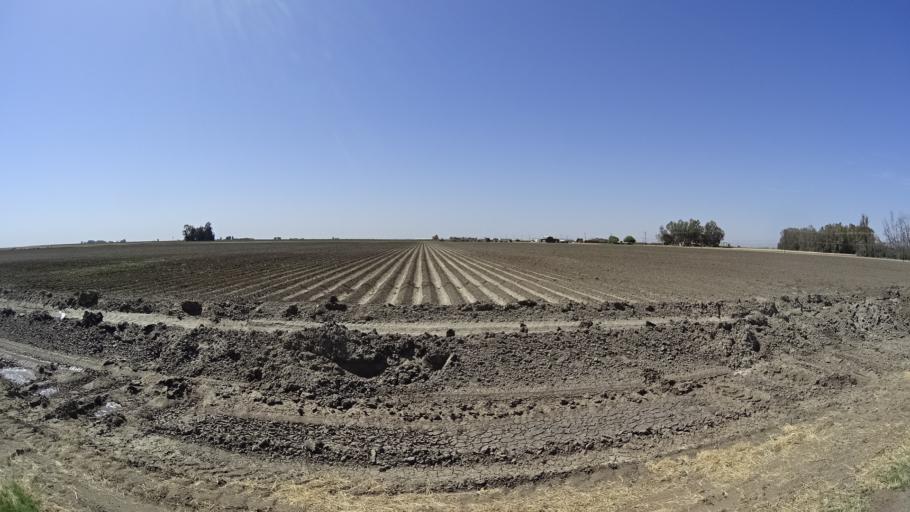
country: US
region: California
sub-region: Kings County
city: Stratford
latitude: 36.1968
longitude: -119.7961
